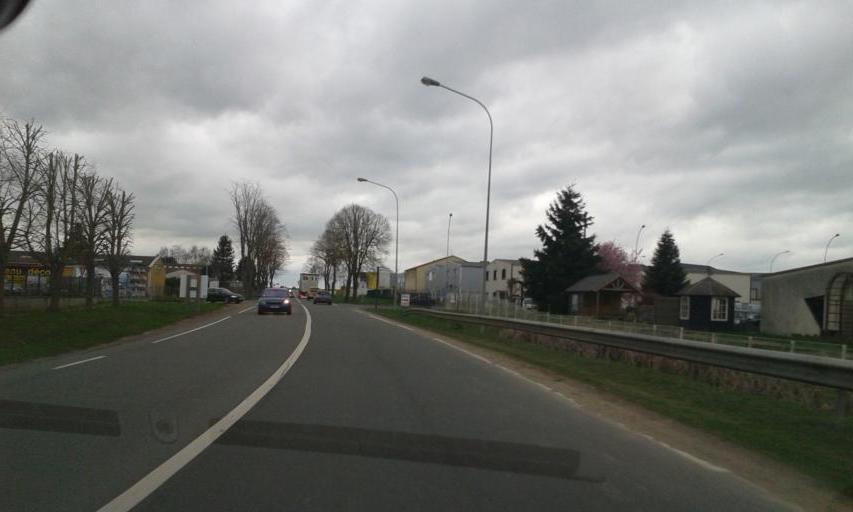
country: FR
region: Centre
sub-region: Departement d'Eure-et-Loir
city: Leves
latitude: 48.4844
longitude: 1.4785
